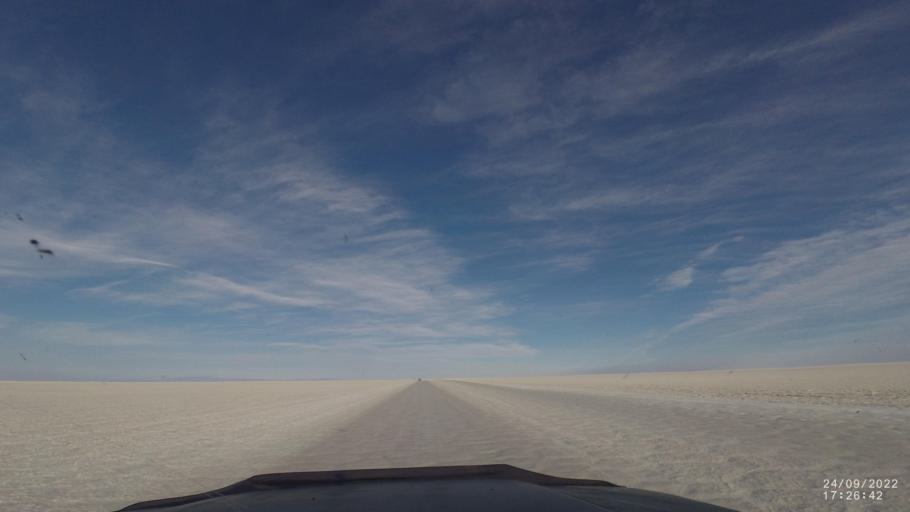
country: BO
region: Potosi
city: Colchani
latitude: -20.2964
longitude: -67.4637
